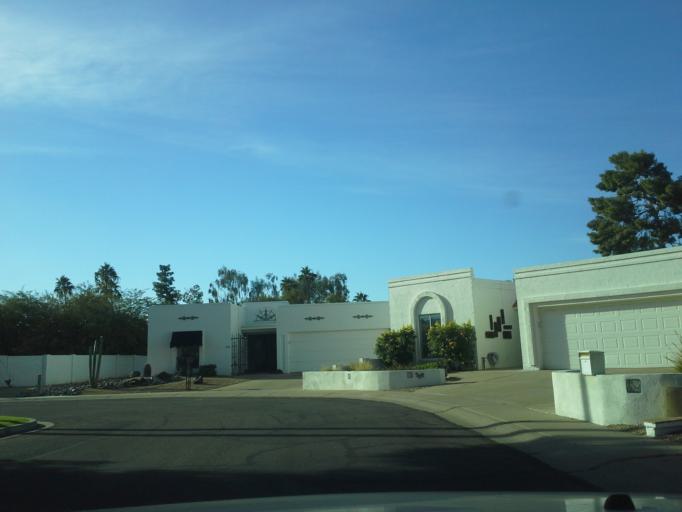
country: US
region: Arizona
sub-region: Maricopa County
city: Glendale
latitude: 33.6145
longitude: -112.0690
